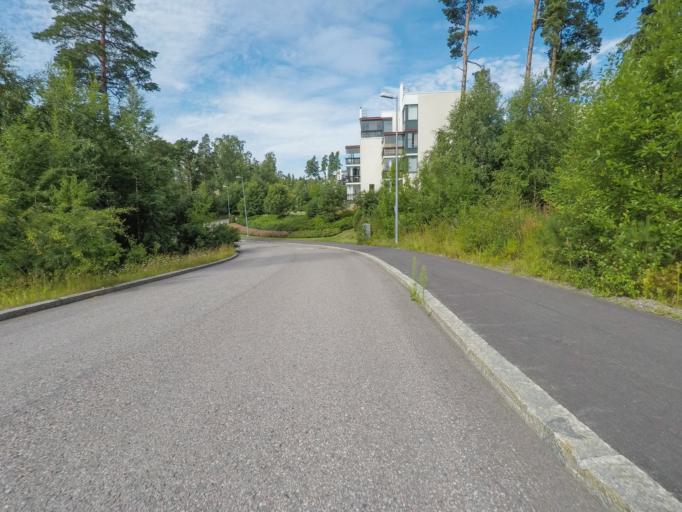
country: FI
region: Uusimaa
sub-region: Helsinki
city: Vantaa
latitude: 60.1606
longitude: 25.0876
